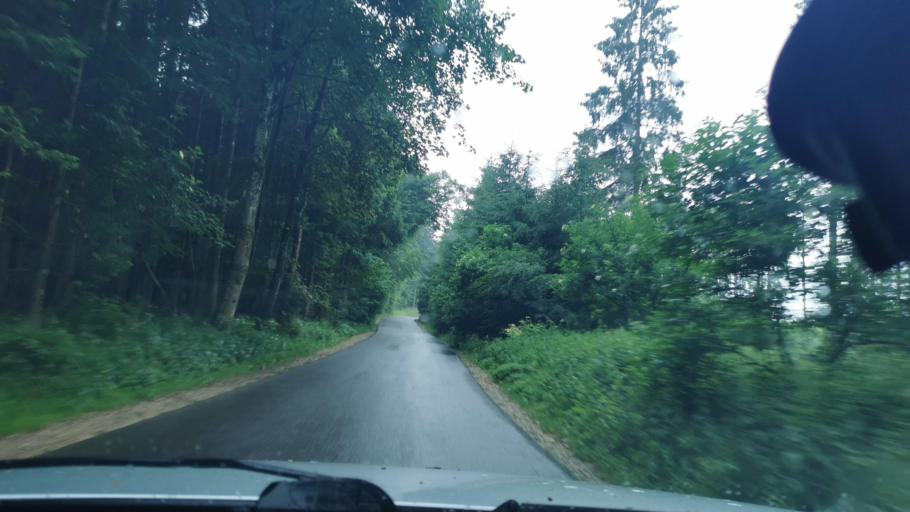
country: DE
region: Baden-Wuerttemberg
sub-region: Regierungsbezirk Stuttgart
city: Bohmenkirch
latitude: 48.7187
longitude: 9.9245
